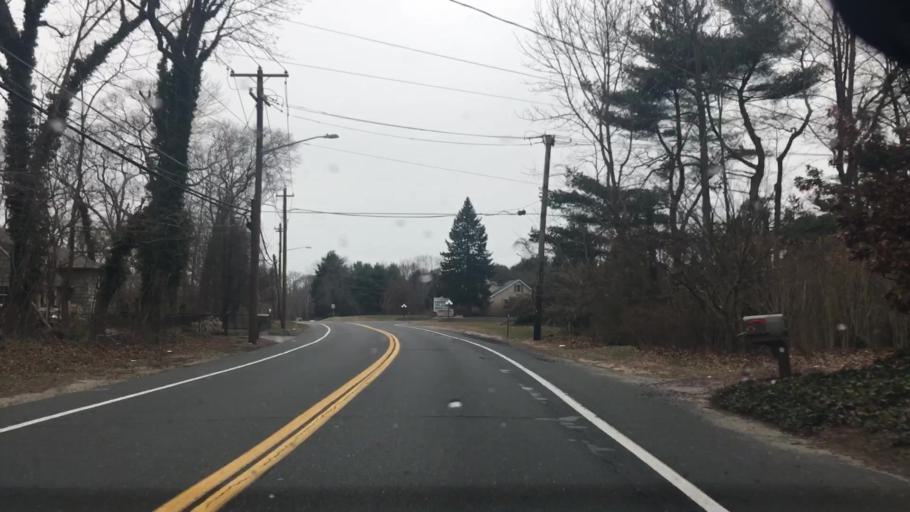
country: US
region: New York
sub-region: Suffolk County
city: Middle Island
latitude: 40.8577
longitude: -72.9386
